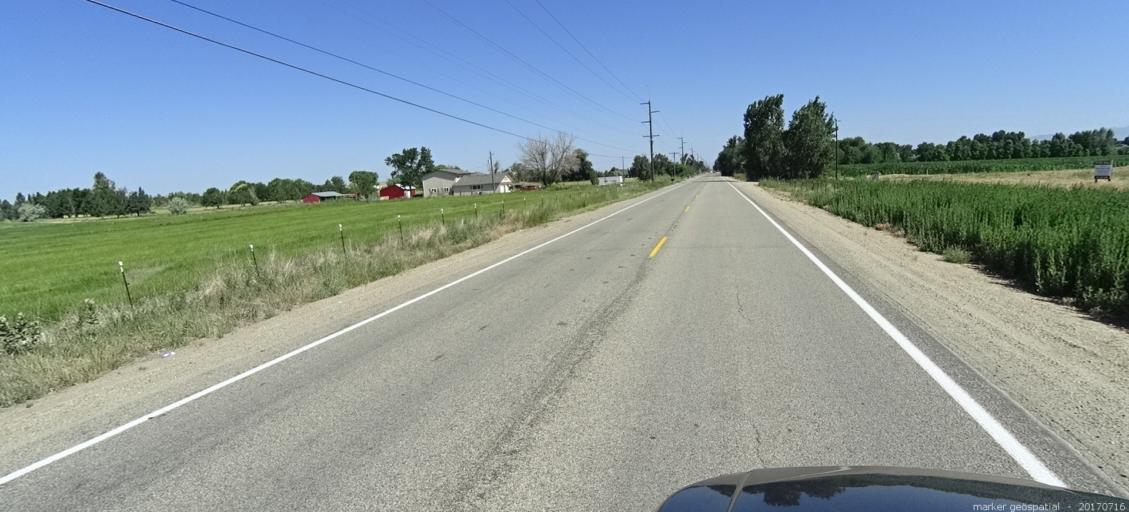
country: US
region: Idaho
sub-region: Ada County
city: Kuna
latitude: 43.5237
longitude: -116.3344
